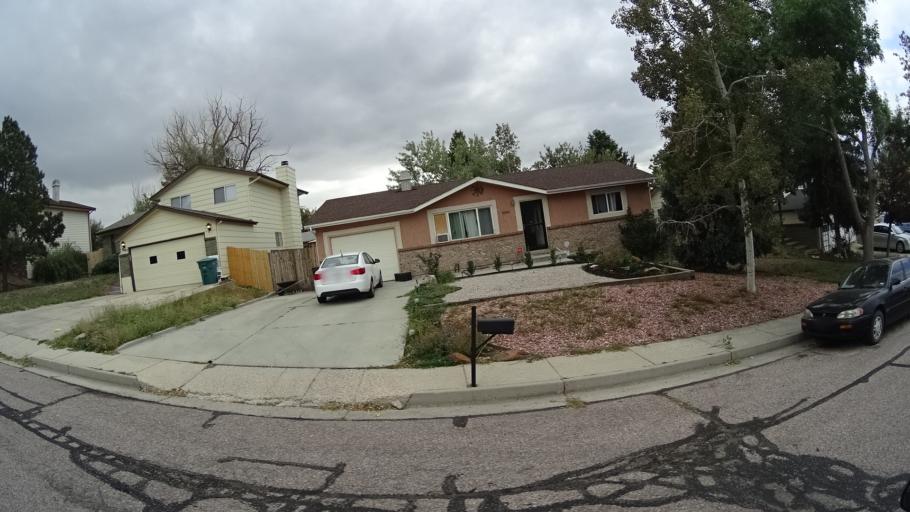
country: US
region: Colorado
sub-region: El Paso County
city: Cimarron Hills
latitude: 38.8903
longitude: -104.7340
